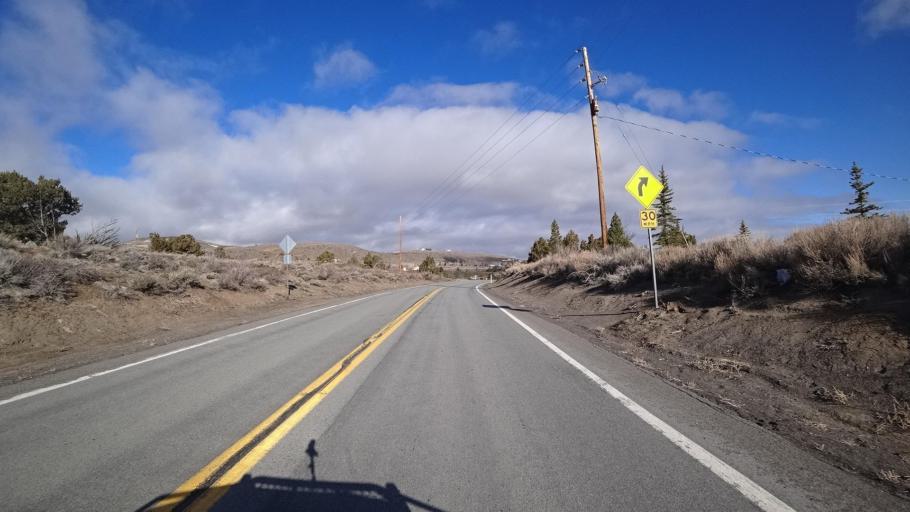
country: US
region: Nevada
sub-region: Washoe County
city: Cold Springs
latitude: 39.7811
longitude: -119.8944
